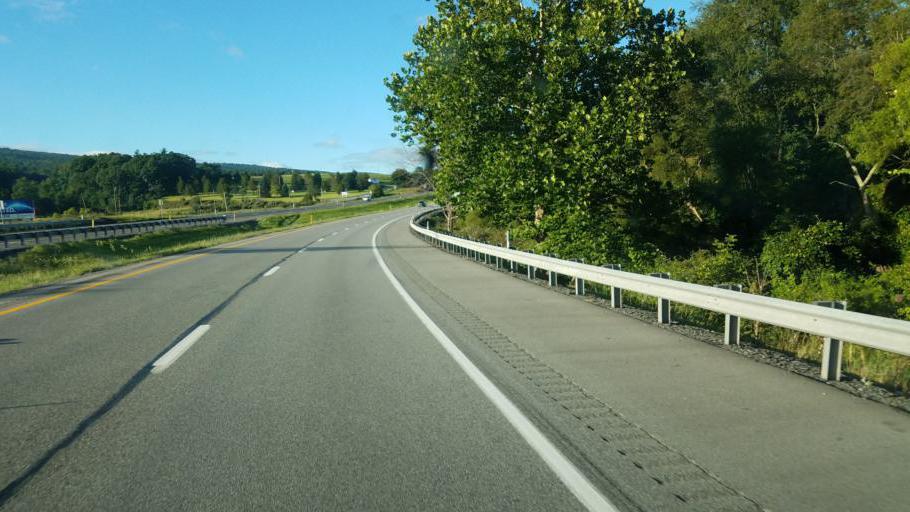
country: US
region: Pennsylvania
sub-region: Bedford County
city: Earlston
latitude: 39.9418
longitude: -78.2273
